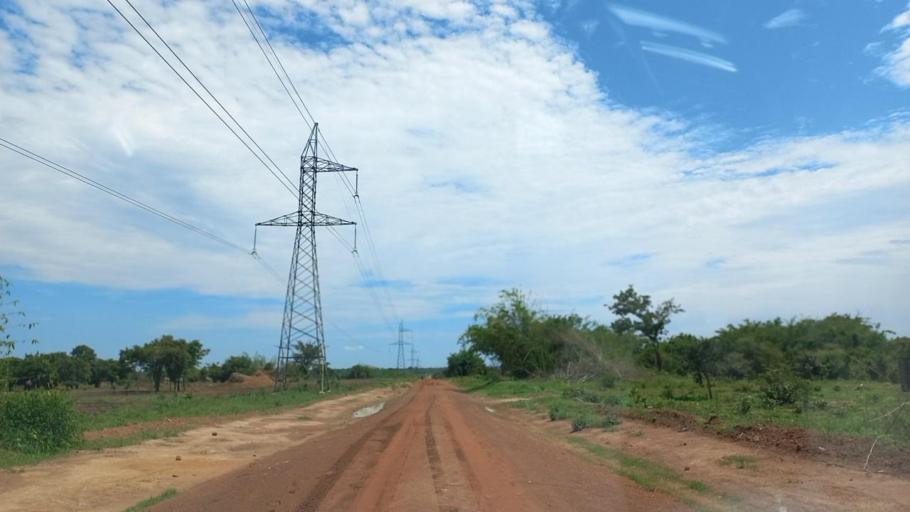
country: ZM
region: Copperbelt
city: Kitwe
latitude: -12.8390
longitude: 28.3408
